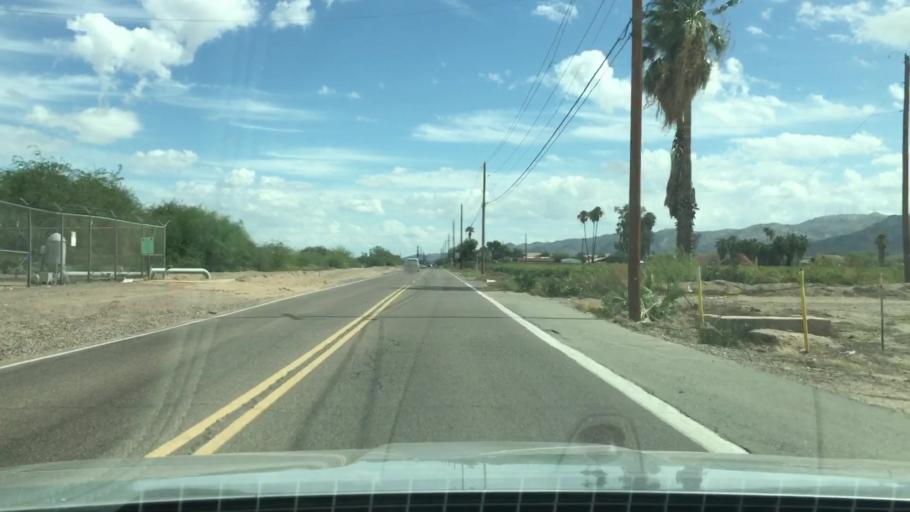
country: US
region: Arizona
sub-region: Maricopa County
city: Laveen
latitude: 33.3630
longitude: -112.1437
